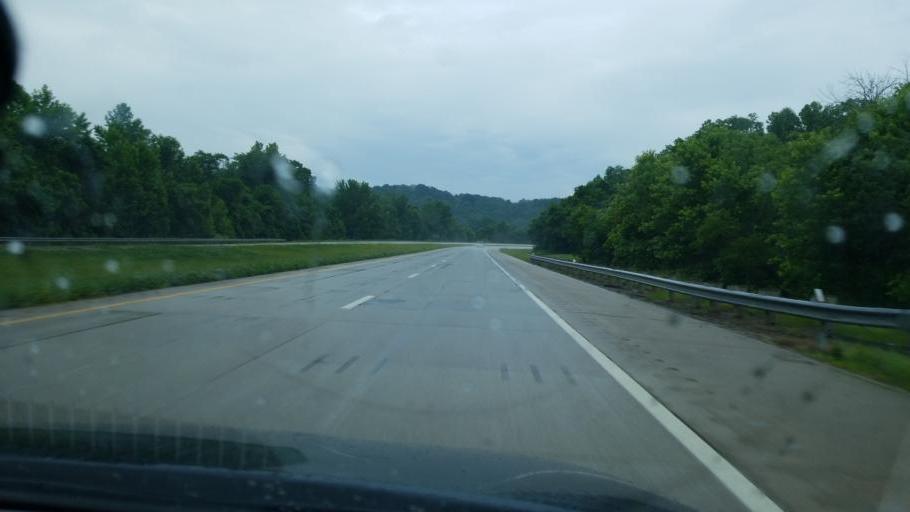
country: US
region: Ohio
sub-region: Athens County
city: Athens
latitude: 39.3061
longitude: -81.9572
